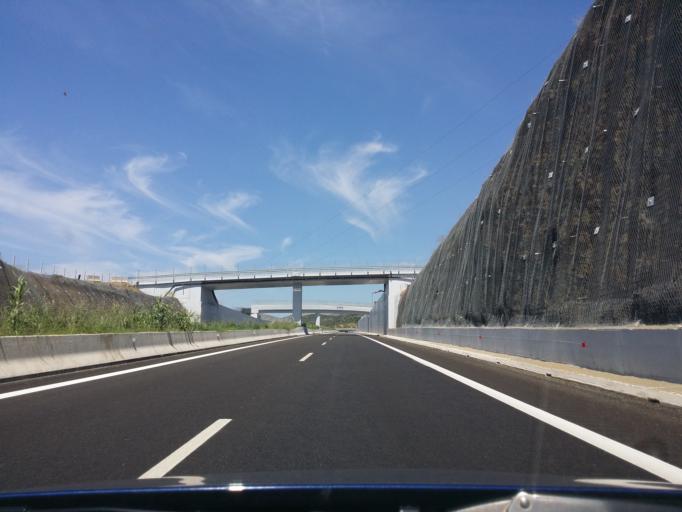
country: GR
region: West Greece
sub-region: Nomos Aitolias kai Akarnanias
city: Mesolongi
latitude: 38.3867
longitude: 21.4840
